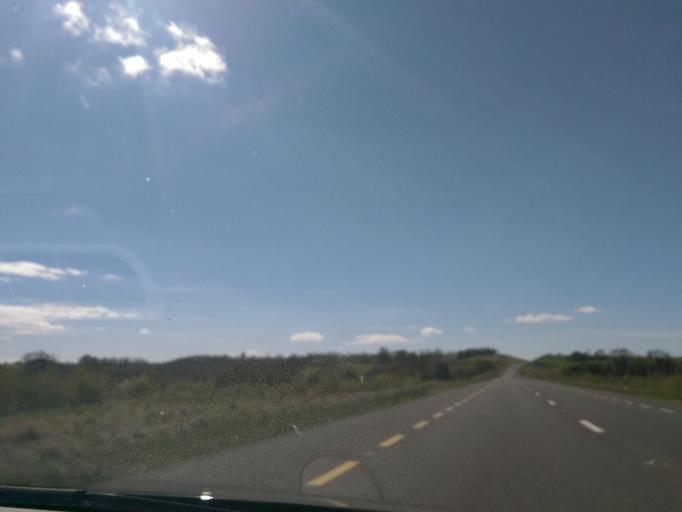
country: IE
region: Leinster
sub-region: Kildare
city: Moone
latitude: 53.0019
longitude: -6.8129
